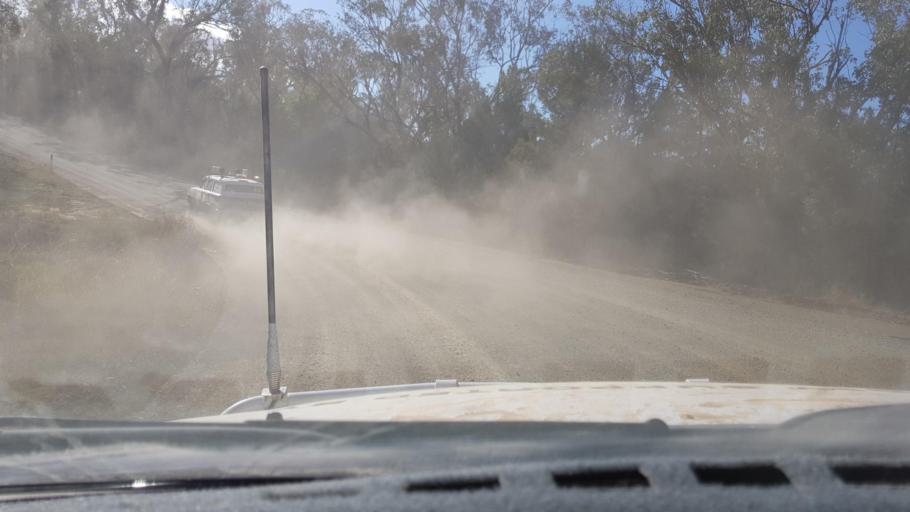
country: AU
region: New South Wales
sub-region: Tamworth Municipality
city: Manilla
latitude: -30.6529
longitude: 150.4931
